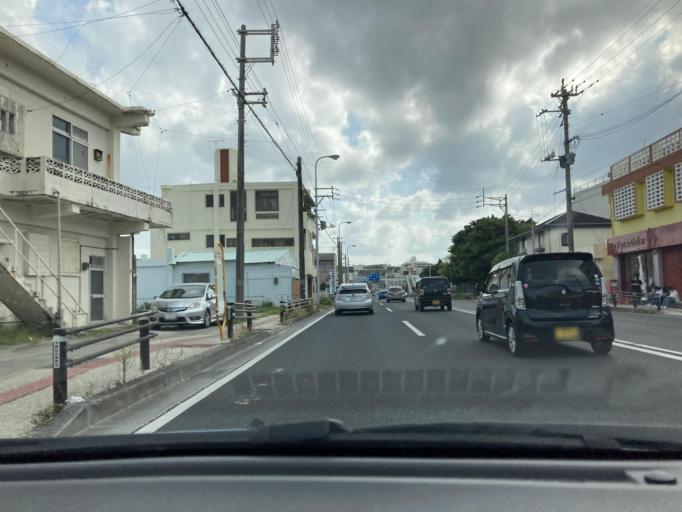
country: JP
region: Okinawa
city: Ginowan
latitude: 26.2051
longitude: 127.7558
